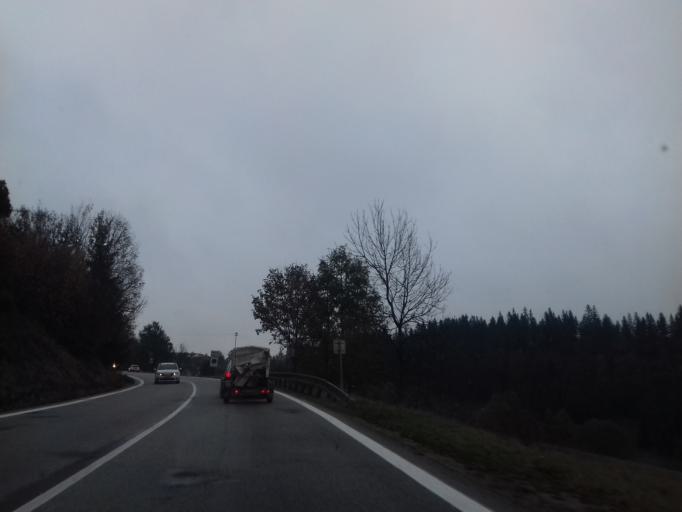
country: SK
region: Banskobystricky
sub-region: Okres Banska Bystrica
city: Banska Bystrica
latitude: 48.8808
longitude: 19.2153
